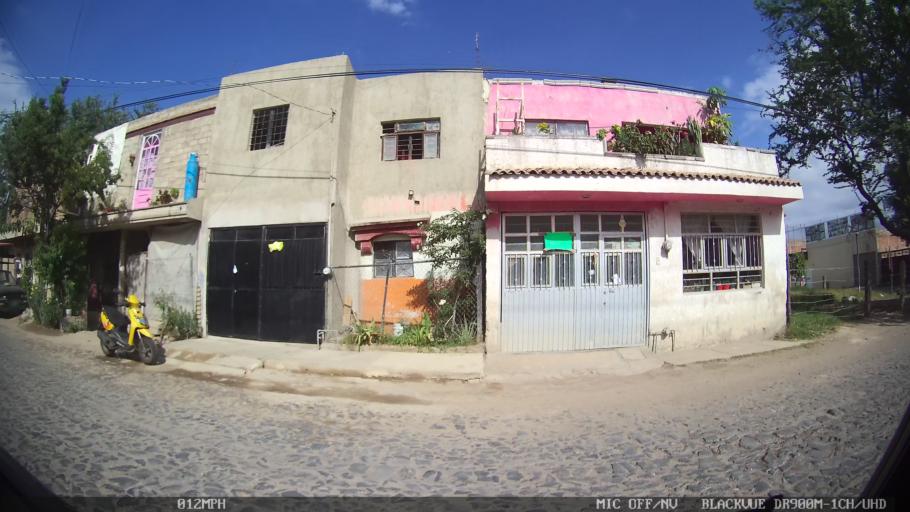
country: MX
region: Jalisco
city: Tonala
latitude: 20.6599
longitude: -103.2530
